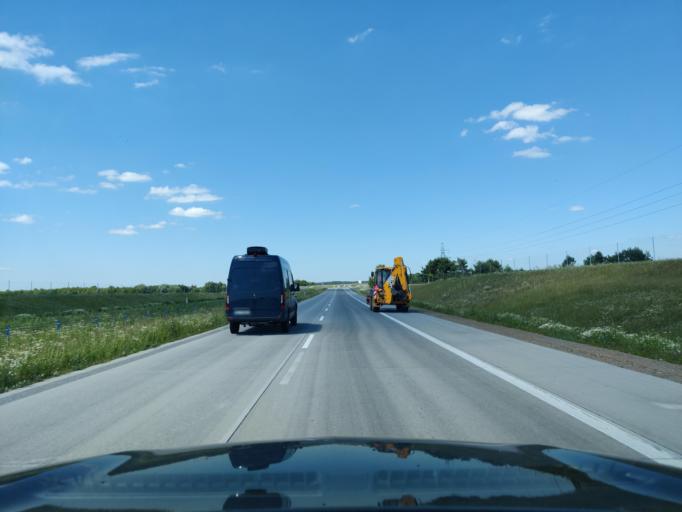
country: PL
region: Masovian Voivodeship
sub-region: Powiat mlawski
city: Mlawa
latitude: 53.1066
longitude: 20.4130
